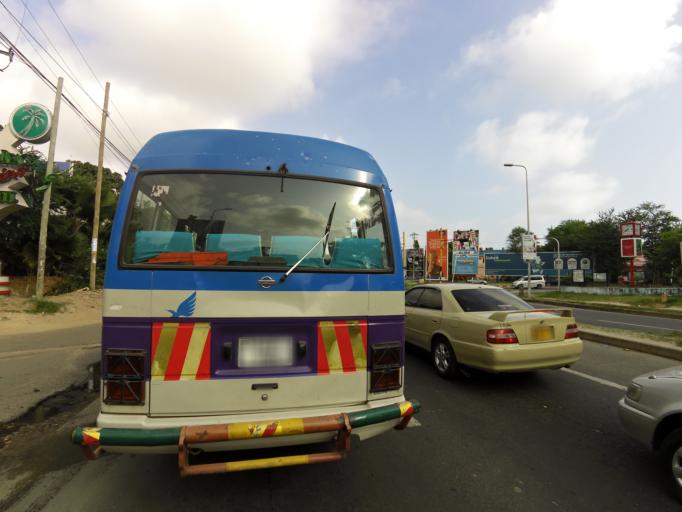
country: TZ
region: Dar es Salaam
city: Dar es Salaam
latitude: -6.7990
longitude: 39.2825
